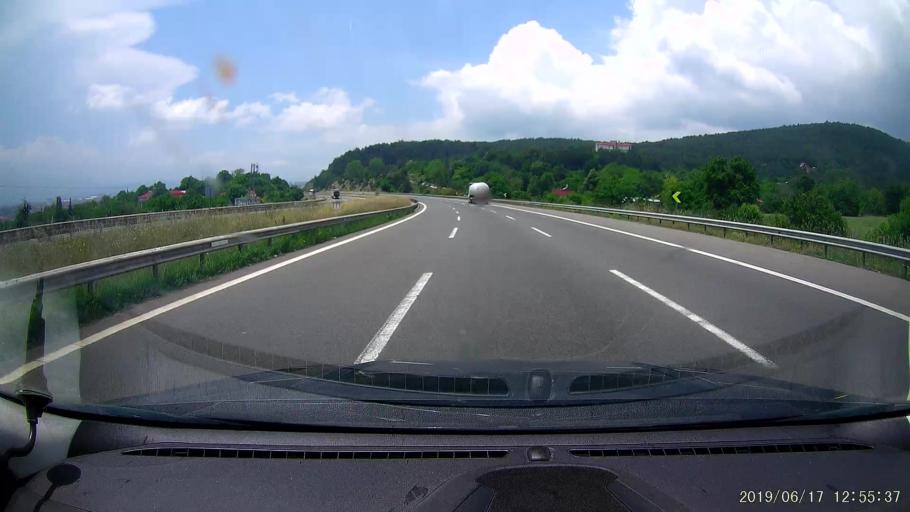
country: TR
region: Bolu
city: Bolu
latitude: 40.7616
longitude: 31.5890
